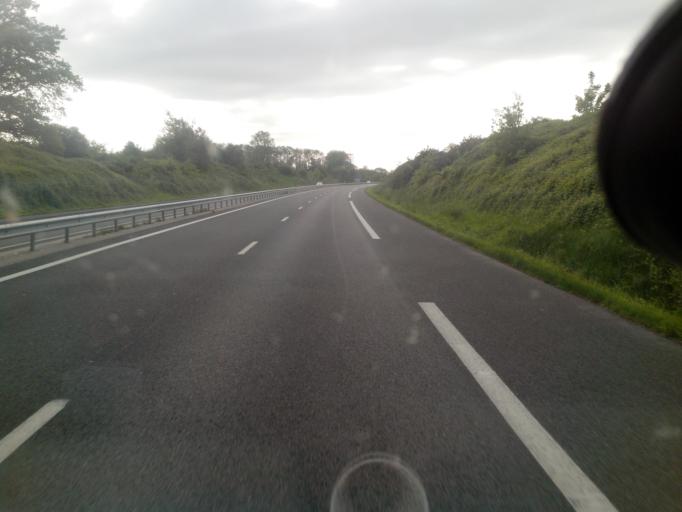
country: FR
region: Haute-Normandie
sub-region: Departement de l'Eure
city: Beuzeville
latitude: 49.3261
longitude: 0.2854
